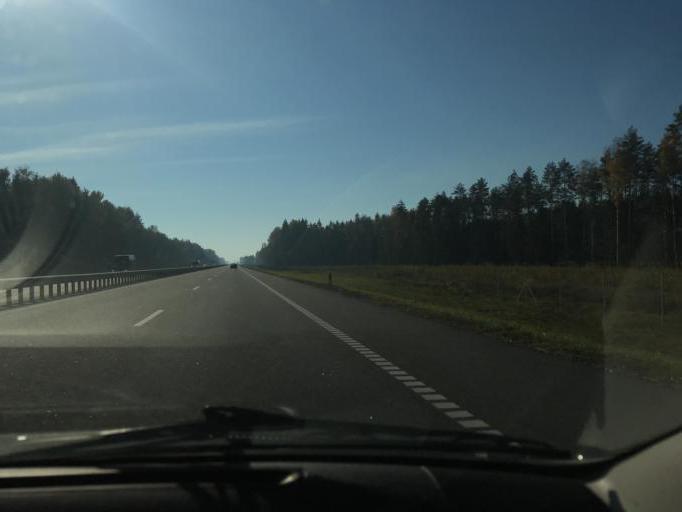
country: BY
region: Minsk
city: Slutsk
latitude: 53.2652
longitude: 27.5501
